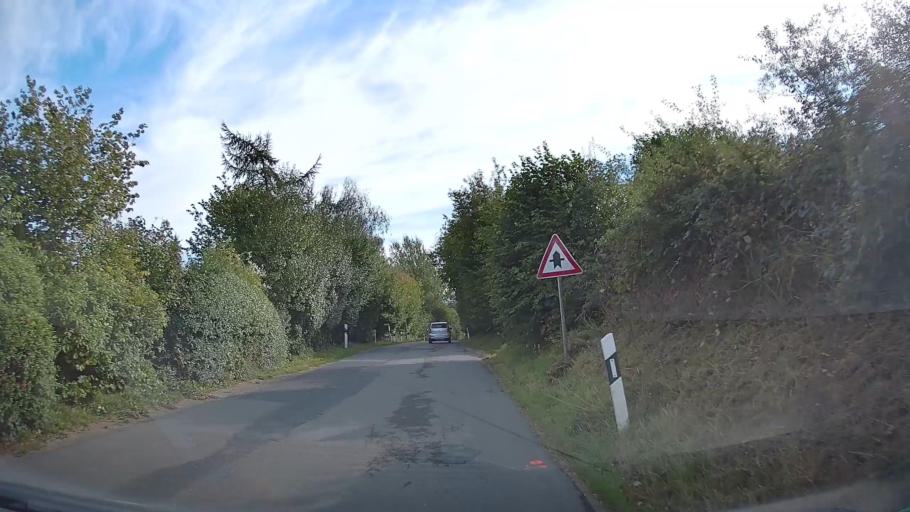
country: DE
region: Schleswig-Holstein
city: Ringsberg
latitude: 54.8392
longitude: 9.5877
